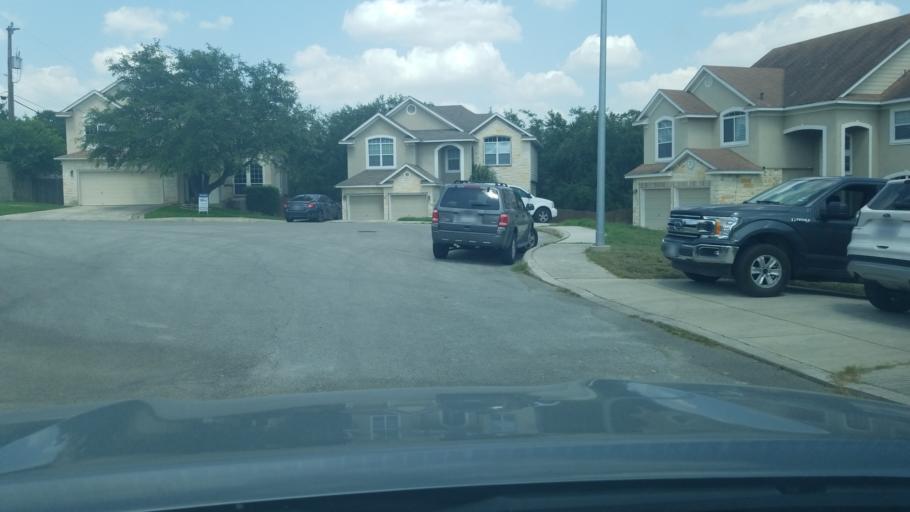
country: US
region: Texas
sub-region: Bexar County
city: Timberwood Park
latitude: 29.6602
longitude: -98.4955
